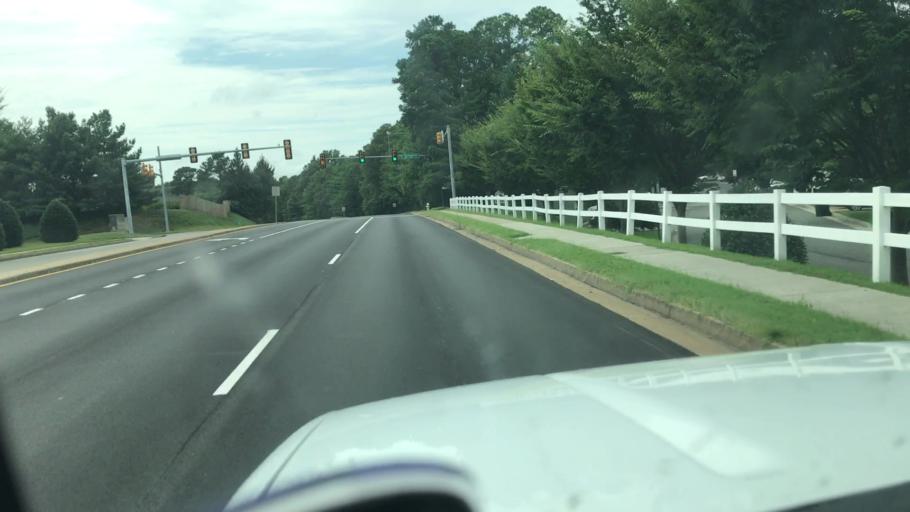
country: US
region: Virginia
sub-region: Henrico County
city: Short Pump
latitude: 37.6245
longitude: -77.5936
